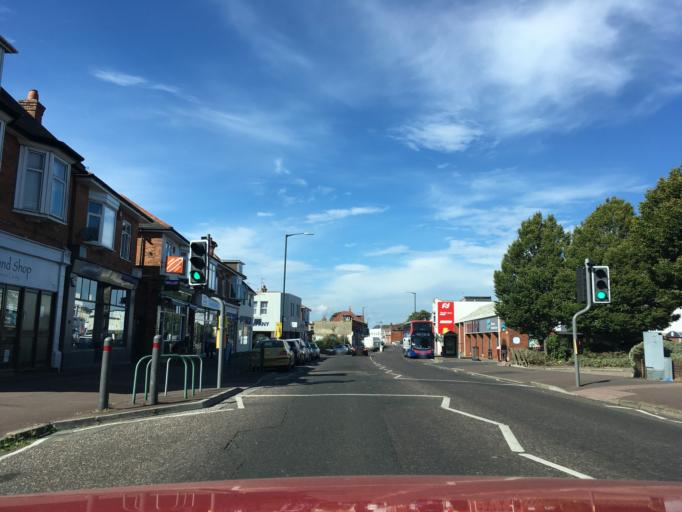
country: GB
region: England
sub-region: Bournemouth
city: Bournemouth
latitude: 50.7548
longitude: -1.8749
